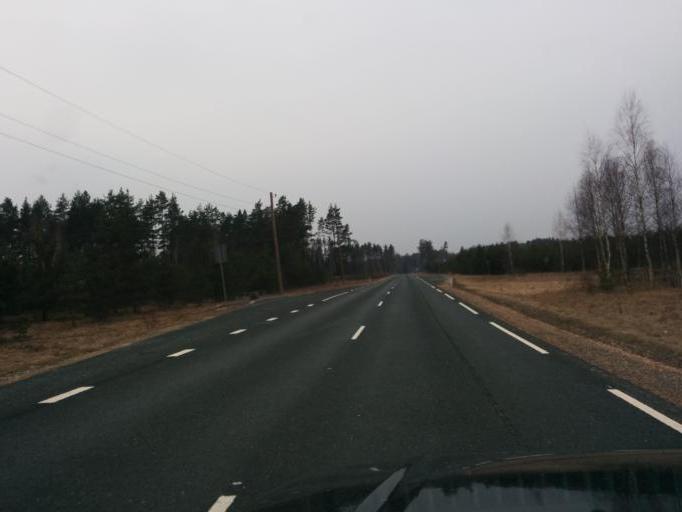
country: LV
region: Ikskile
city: Ikskile
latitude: 56.8031
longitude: 24.5489
